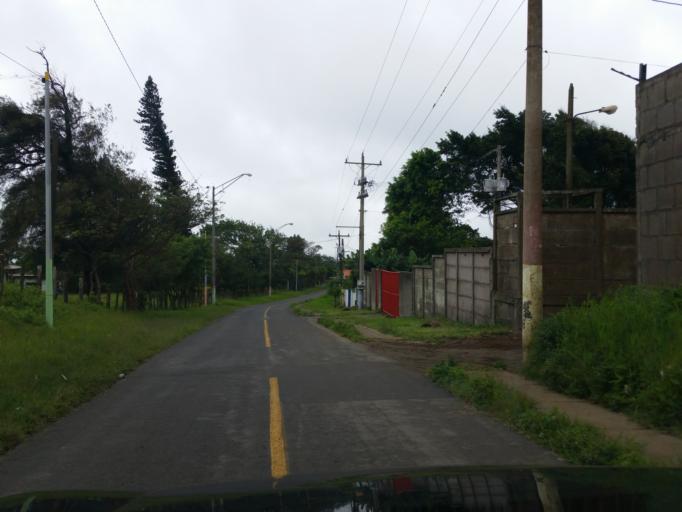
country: NI
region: Managua
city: El Crucero
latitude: 11.9959
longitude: -86.3063
